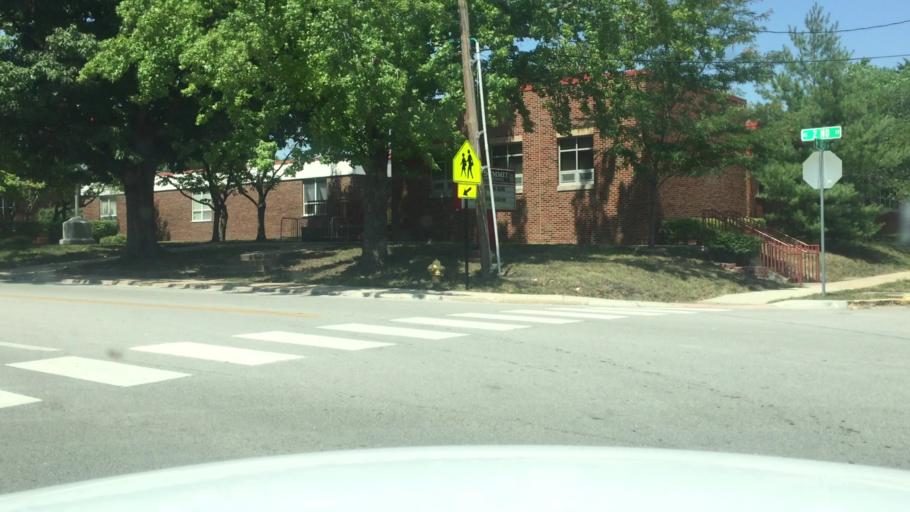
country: US
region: Missouri
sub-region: Jackson County
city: Lees Summit
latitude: 38.9146
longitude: -94.3756
